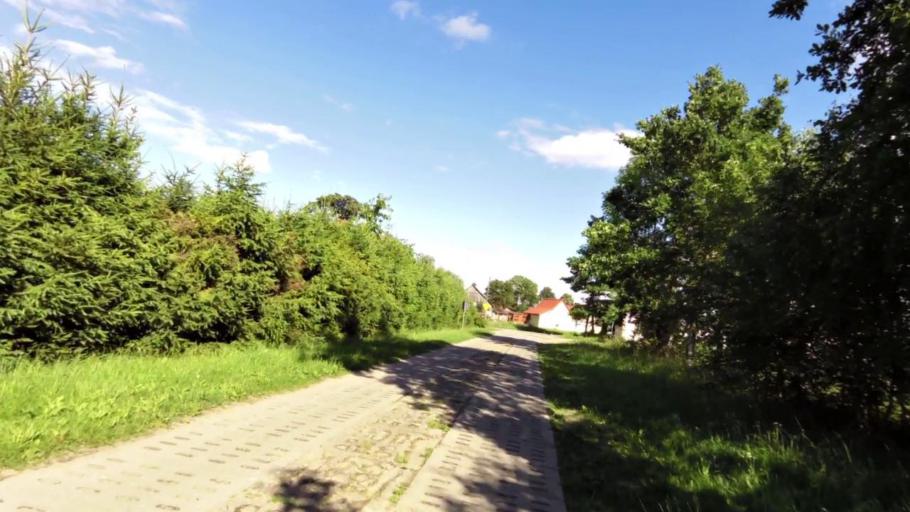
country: PL
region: West Pomeranian Voivodeship
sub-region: Powiat slawienski
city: Slawno
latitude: 54.4604
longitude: 16.7340
